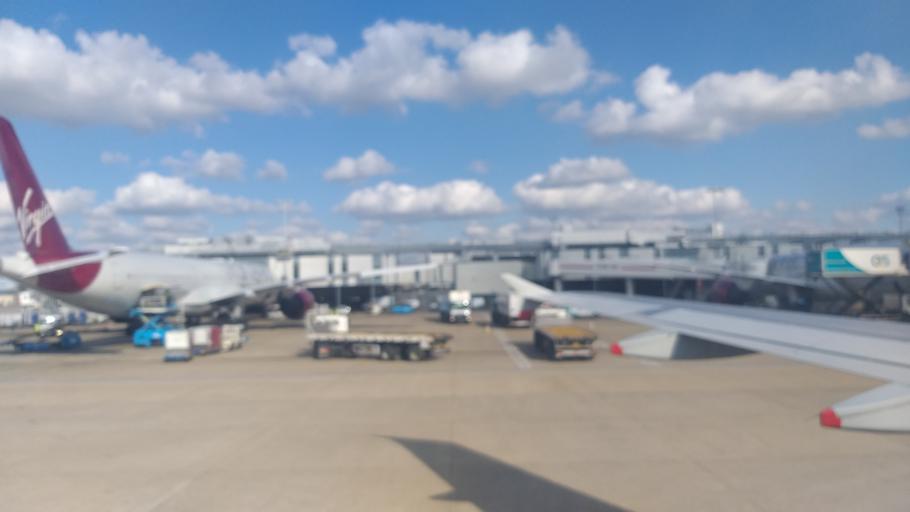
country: GB
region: England
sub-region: Greater London
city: West Drayton
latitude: 51.4695
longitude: -0.4660
